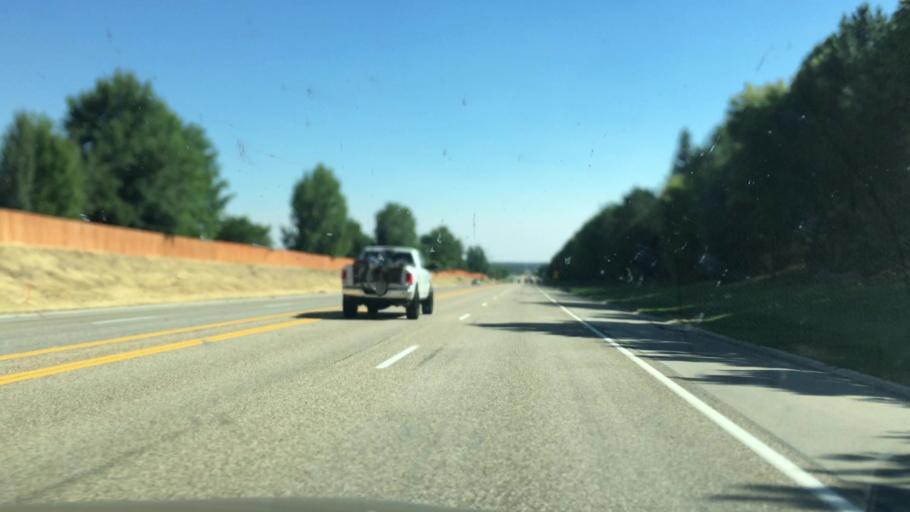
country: US
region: Idaho
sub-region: Ada County
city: Eagle
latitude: 43.7116
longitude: -116.3189
